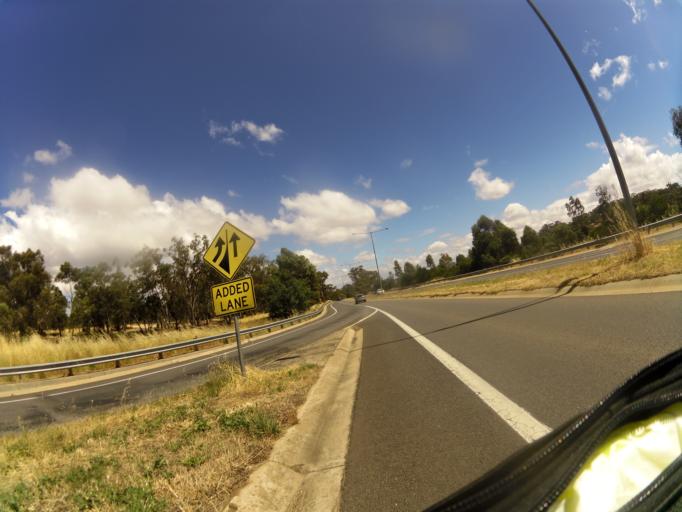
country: AU
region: Victoria
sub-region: Mount Alexander
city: Castlemaine
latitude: -37.0054
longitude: 144.2480
